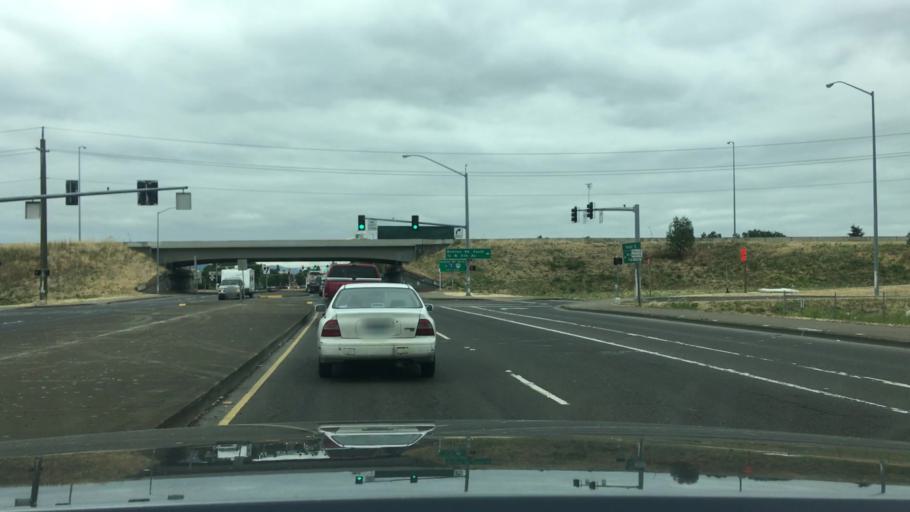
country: US
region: Oregon
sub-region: Lane County
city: Eugene
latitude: 44.0844
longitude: -123.1740
